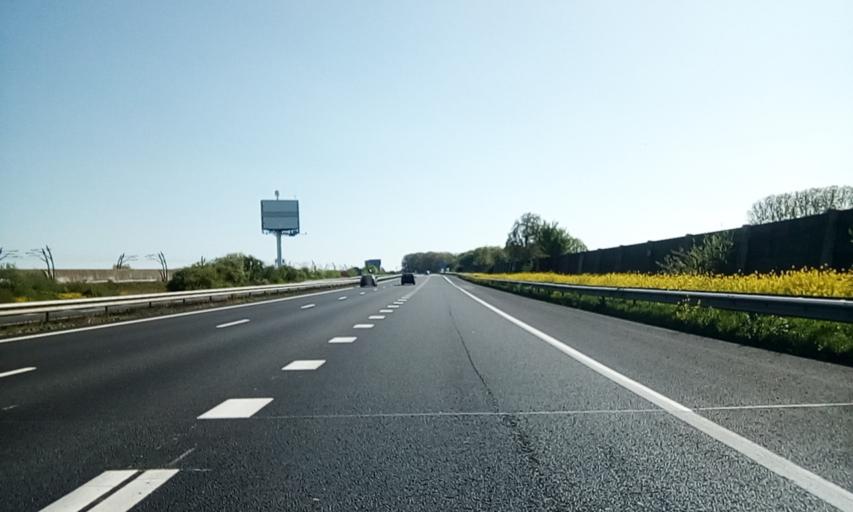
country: NL
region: Gelderland
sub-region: Gemeente Tiel
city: Tiel
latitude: 51.9012
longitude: 5.4378
